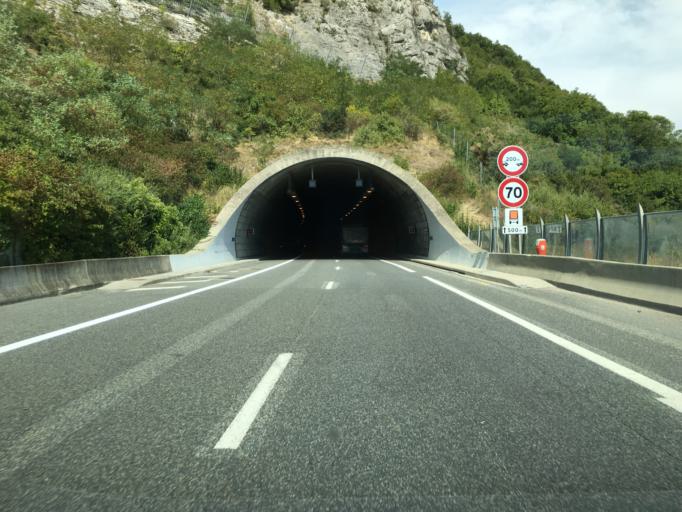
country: FR
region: Rhone-Alpes
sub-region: Departement de l'Isere
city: Allieres-et-Risset
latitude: 45.0805
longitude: 5.6793
